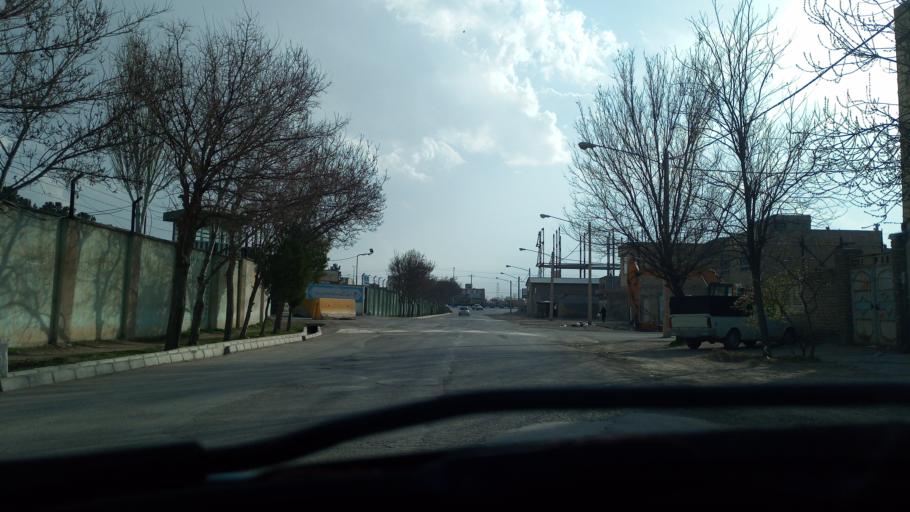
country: IR
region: Razavi Khorasan
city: Quchan
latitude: 37.1012
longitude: 58.4962
